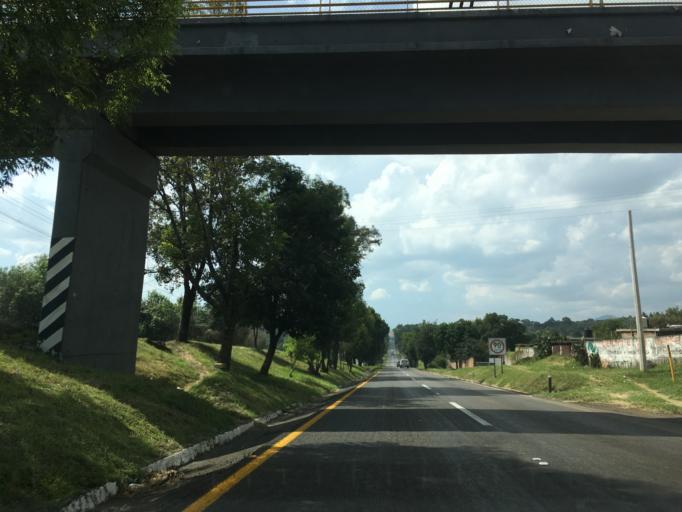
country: MX
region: Michoacan
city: Lagunillas
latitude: 19.5556
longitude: -101.3896
